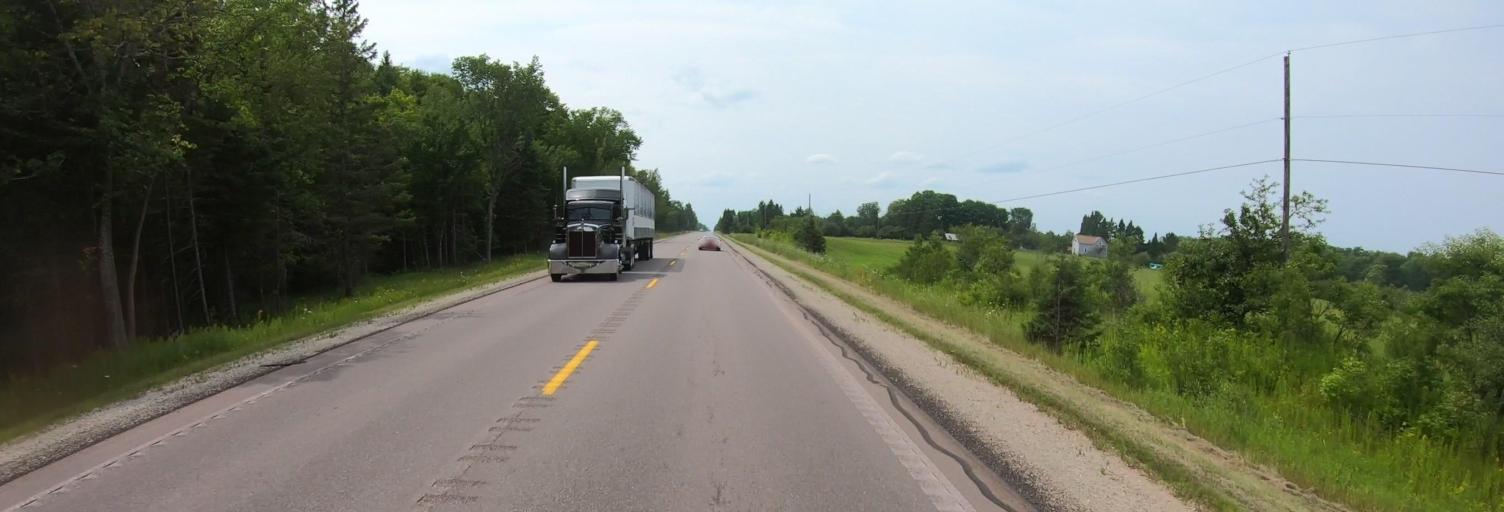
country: US
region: Michigan
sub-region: Marquette County
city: K. I. Sawyer Air Force Base
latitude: 46.3476
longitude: -87.1441
